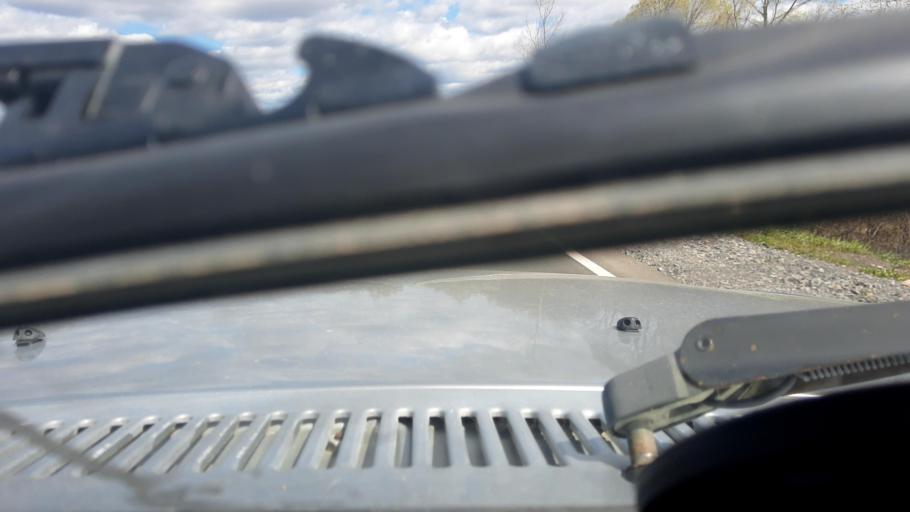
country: RU
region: Bashkortostan
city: Yazykovo
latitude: 55.2995
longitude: 56.3030
